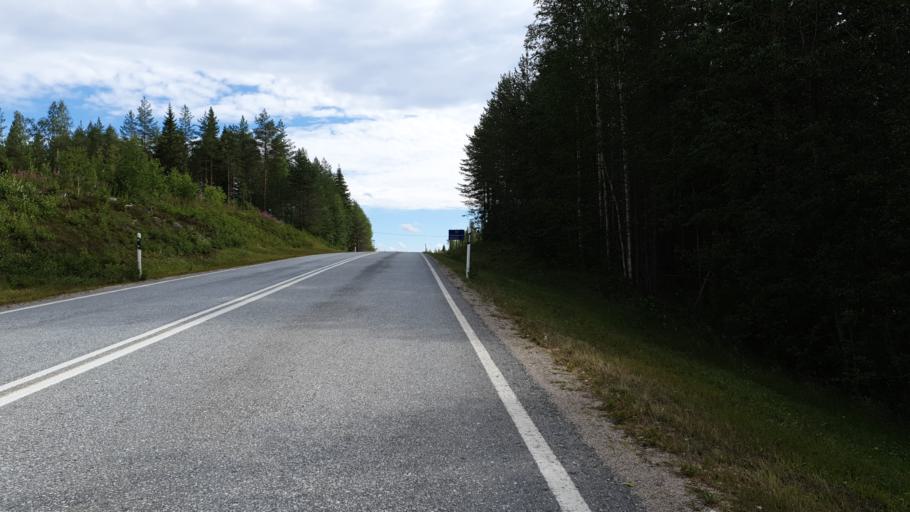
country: FI
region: Kainuu
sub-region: Kehys-Kainuu
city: Kuhmo
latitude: 64.4948
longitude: 29.9043
